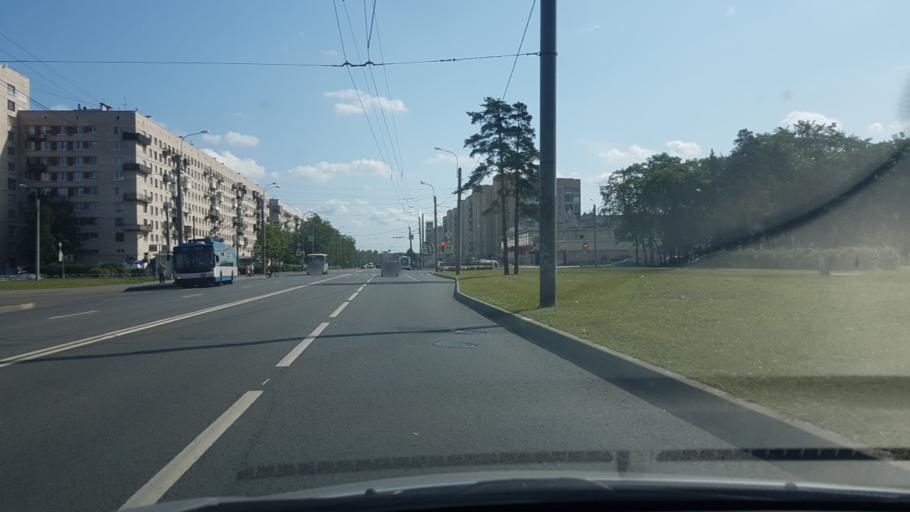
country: RU
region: St.-Petersburg
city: Sosnovaya Polyana
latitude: 59.8353
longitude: 30.1383
